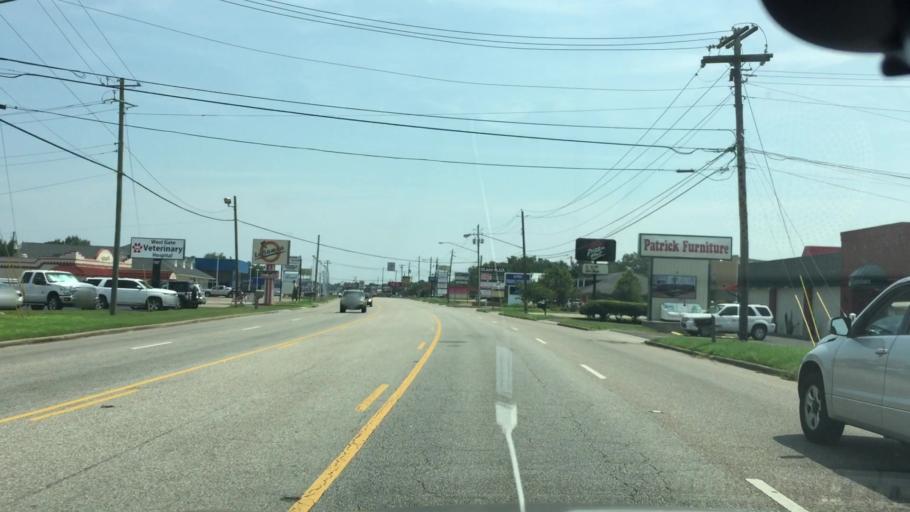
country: US
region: Alabama
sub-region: Coffee County
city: Enterprise
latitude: 31.3245
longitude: -85.8247
